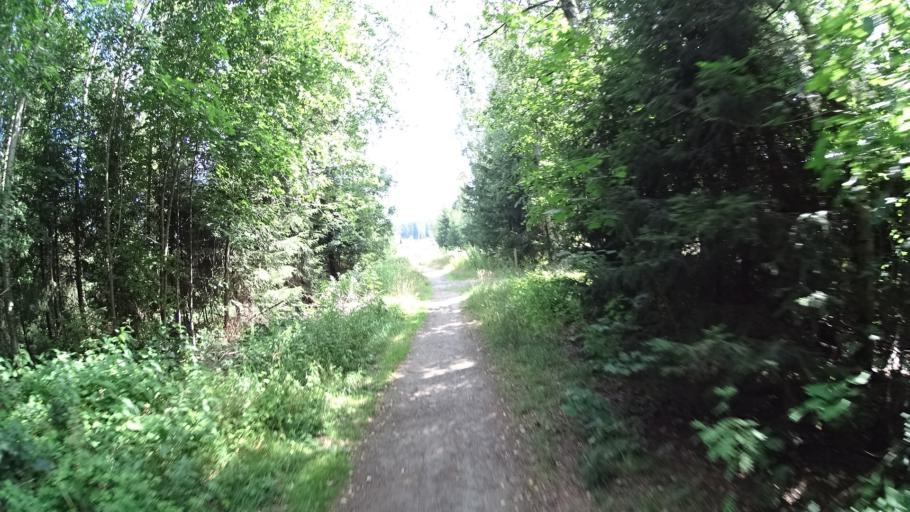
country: FI
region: Uusimaa
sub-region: Porvoo
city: Porvoo
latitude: 60.3885
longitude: 25.7086
